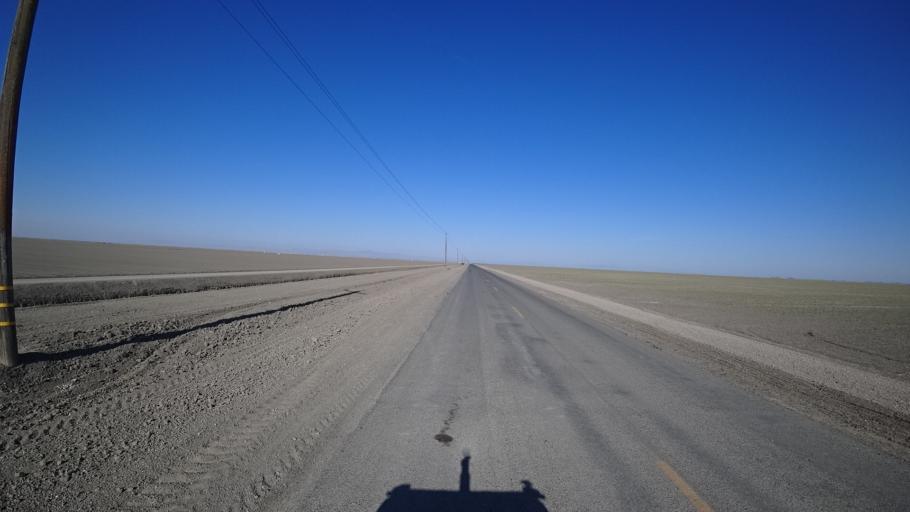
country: US
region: California
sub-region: Kings County
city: Stratford
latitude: 36.0797
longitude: -119.7188
